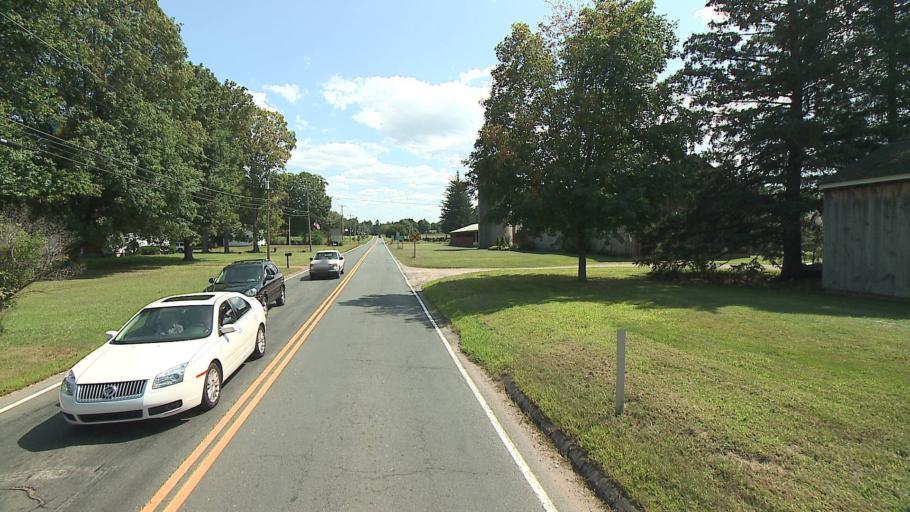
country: US
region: Connecticut
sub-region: Hartford County
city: Broad Brook
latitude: 41.9376
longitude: -72.5270
